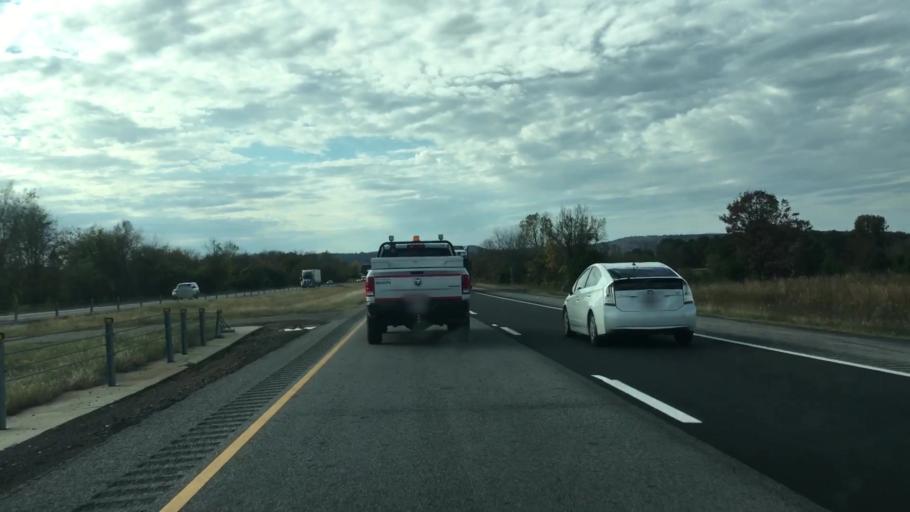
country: US
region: Arkansas
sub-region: Pope County
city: Atkins
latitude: 35.2494
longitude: -92.8810
